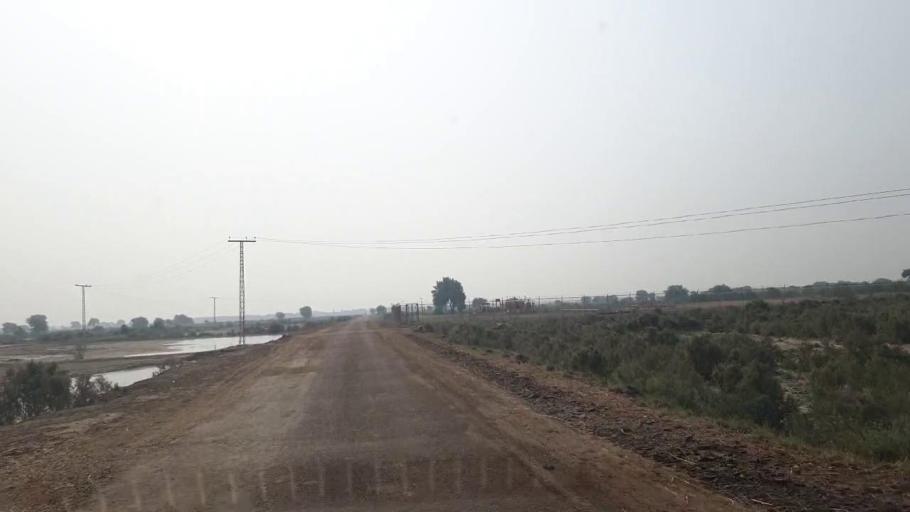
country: PK
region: Sindh
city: Matli
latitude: 25.1395
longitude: 68.6907
